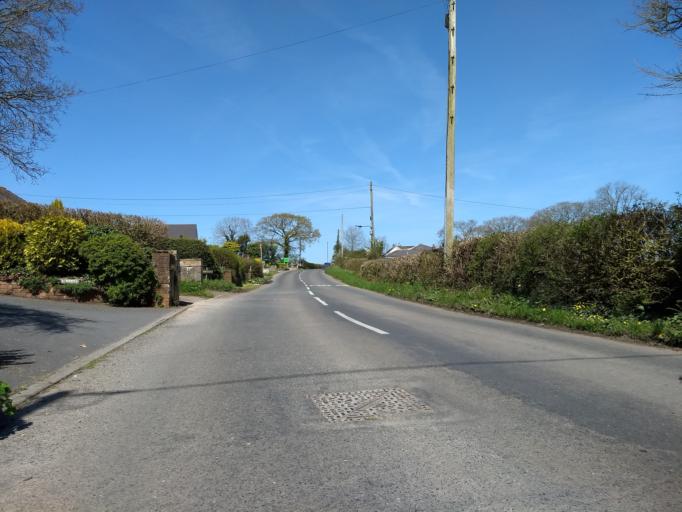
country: GB
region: England
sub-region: Isle of Wight
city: Gurnard
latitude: 50.7411
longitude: -1.3345
